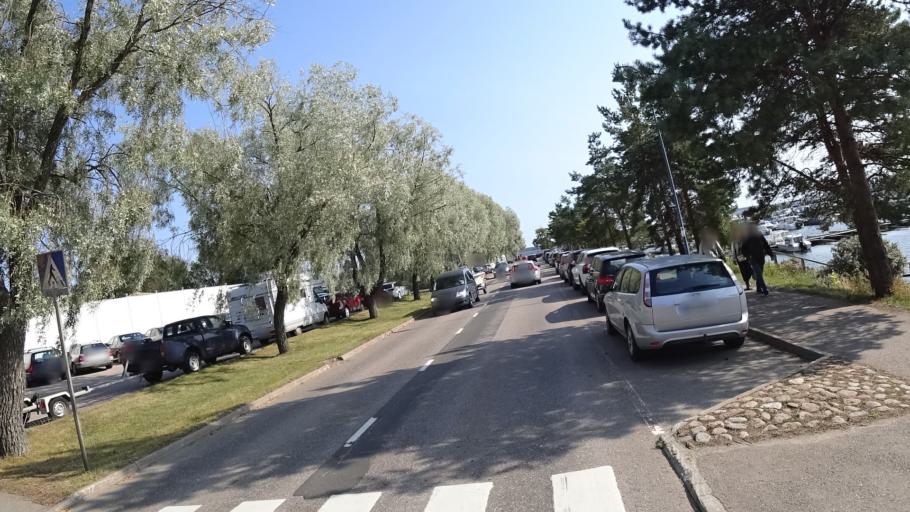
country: FI
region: Kymenlaakso
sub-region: Kotka-Hamina
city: Kotka
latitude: 60.4600
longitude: 26.9533
